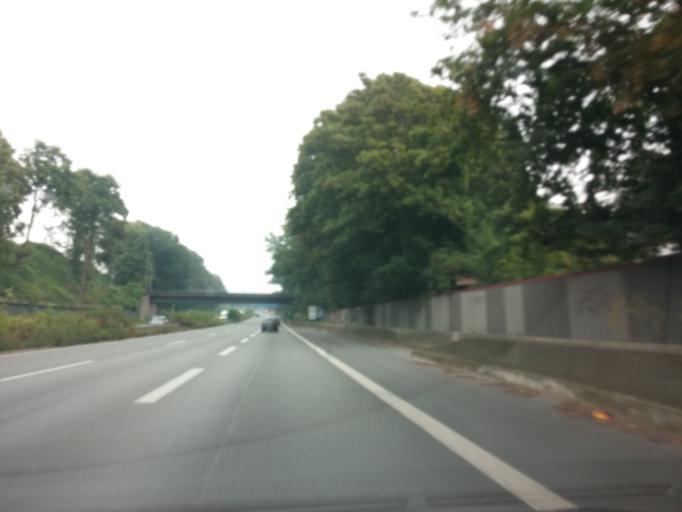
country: DE
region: North Rhine-Westphalia
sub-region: Regierungsbezirk Arnsberg
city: Herne
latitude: 51.5437
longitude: 7.1873
